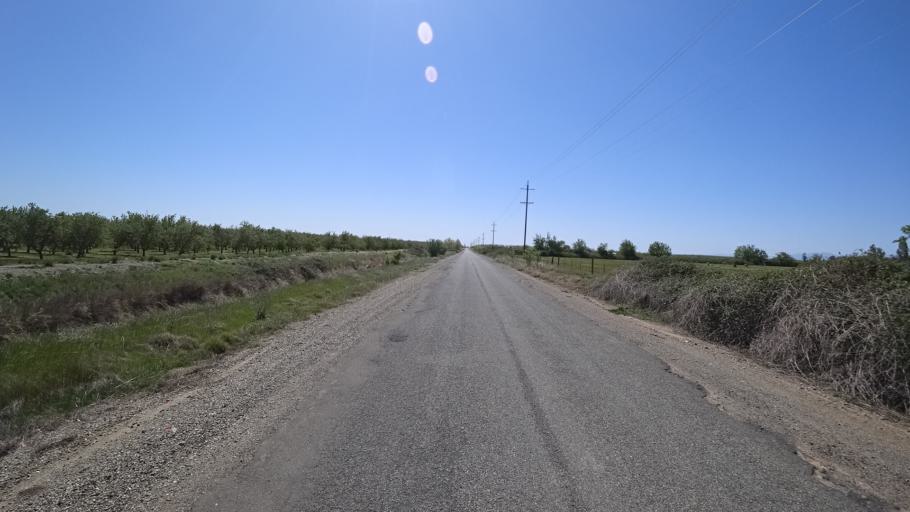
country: US
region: California
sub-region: Glenn County
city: Orland
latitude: 39.7935
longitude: -122.1410
